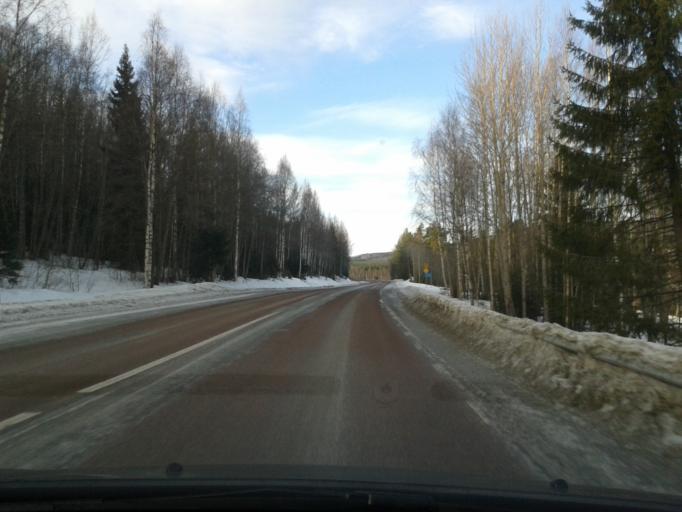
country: SE
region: Vaesternorrland
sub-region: OErnskoeldsviks Kommun
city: Bjasta
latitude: 63.3435
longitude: 18.5030
